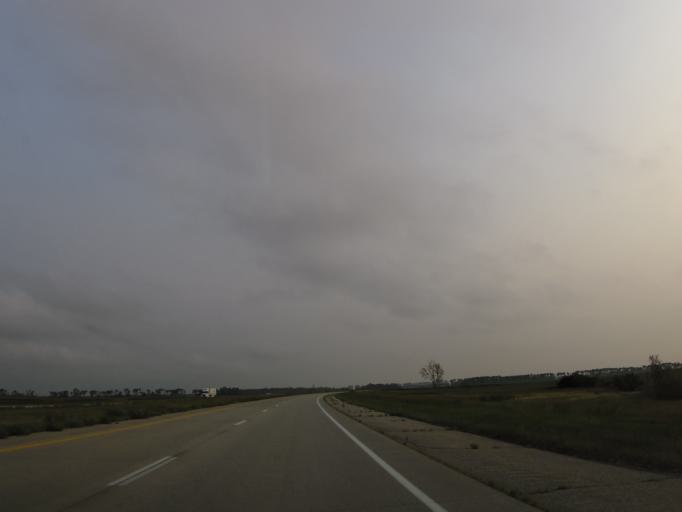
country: US
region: North Dakota
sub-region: Walsh County
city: Grafton
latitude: 48.4703
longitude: -97.1909
